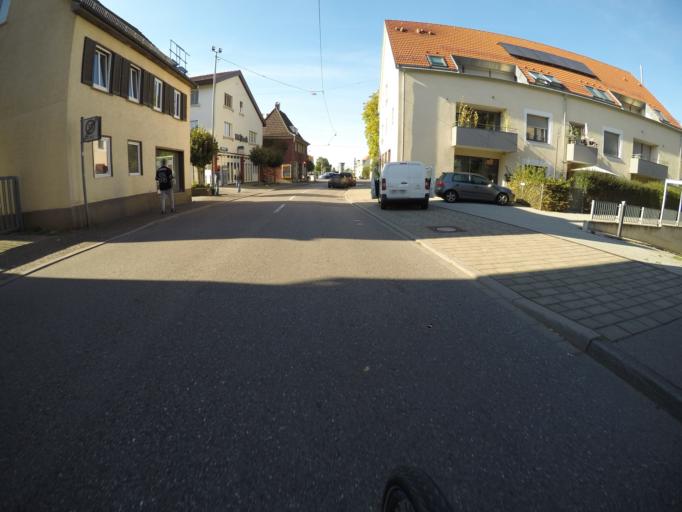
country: DE
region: Baden-Wuerttemberg
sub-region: Regierungsbezirk Stuttgart
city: Ostfildern
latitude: 48.7591
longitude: 9.2551
